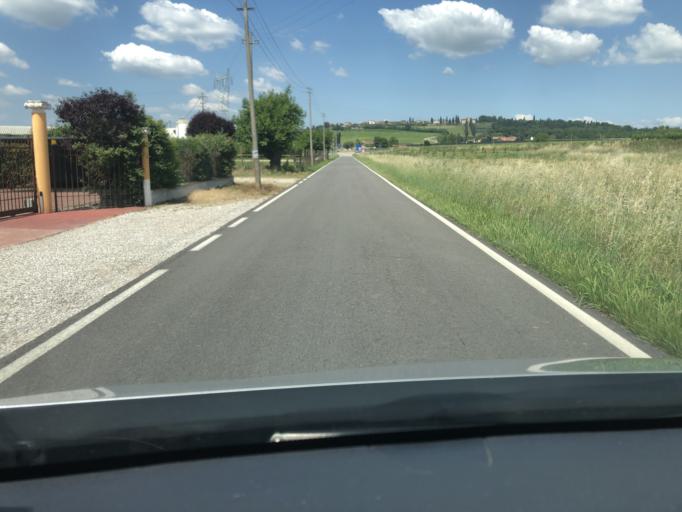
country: IT
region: Veneto
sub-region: Provincia di Verona
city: Rosegaferro
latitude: 45.3622
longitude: 10.8077
